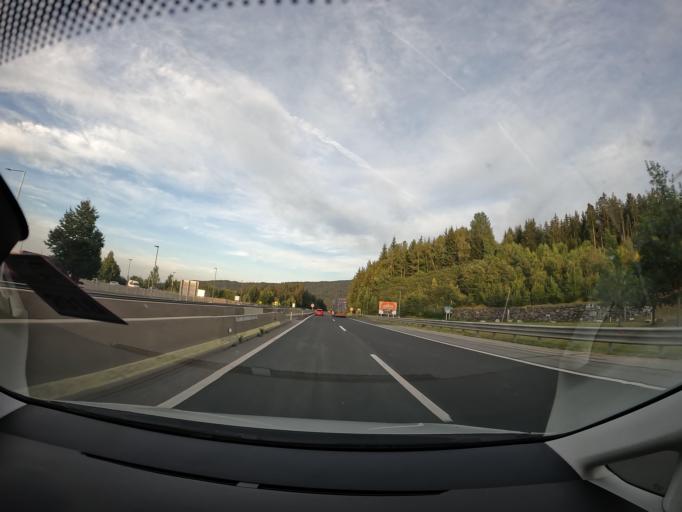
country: AT
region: Styria
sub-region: Politischer Bezirk Voitsberg
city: Voitsberg
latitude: 46.9898
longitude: 15.1105
